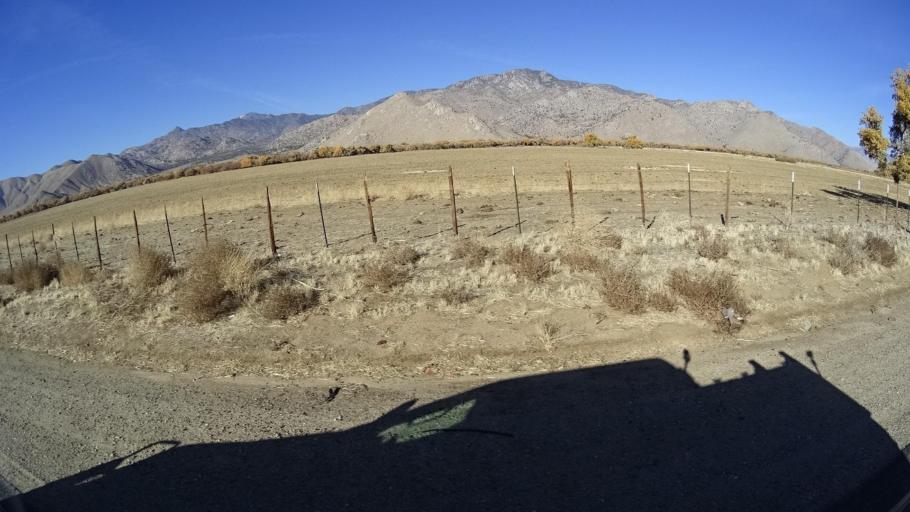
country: US
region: California
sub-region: Kern County
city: Weldon
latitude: 35.6670
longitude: -118.2743
